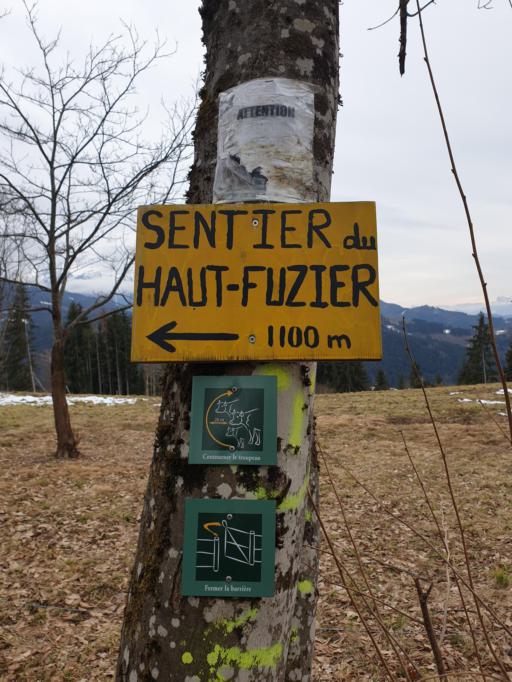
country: FR
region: Rhone-Alpes
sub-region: Departement de l'Isere
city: Le Champ-pres-Froges
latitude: 45.2580
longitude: 5.9557
